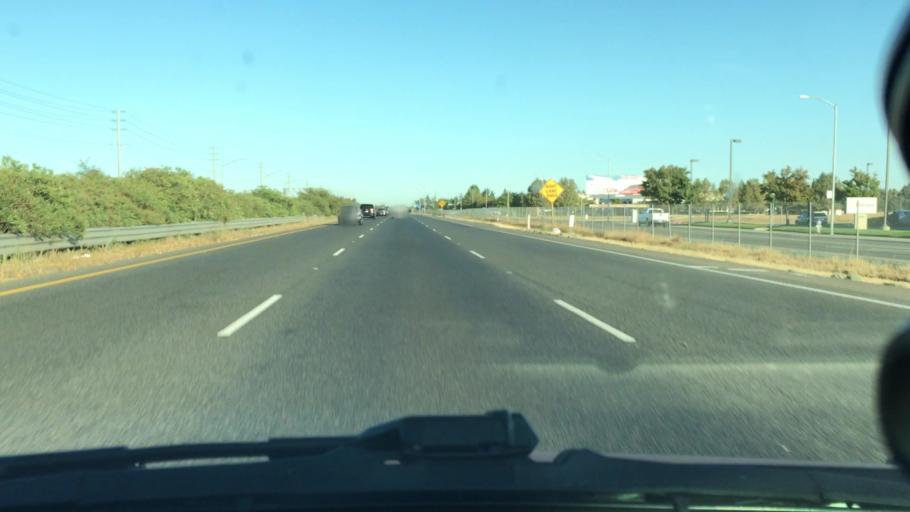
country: US
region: California
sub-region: Sacramento County
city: Elk Grove
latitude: 38.3810
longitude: -121.3665
